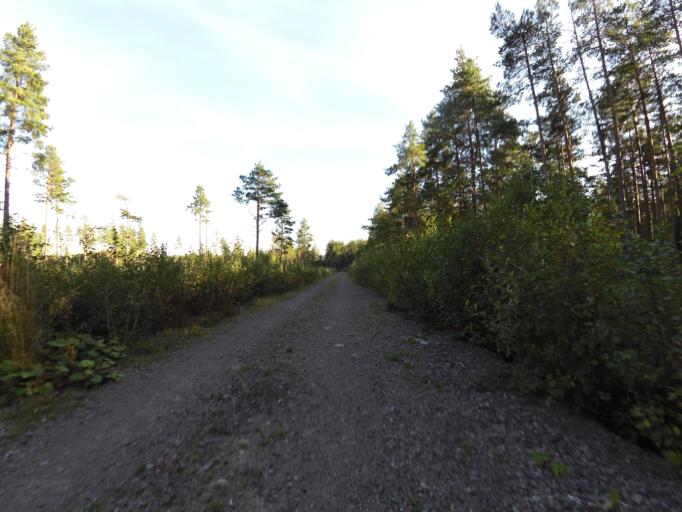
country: SE
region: Gaevleborg
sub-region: Gavle Kommun
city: Gavle
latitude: 60.6414
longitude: 17.1098
